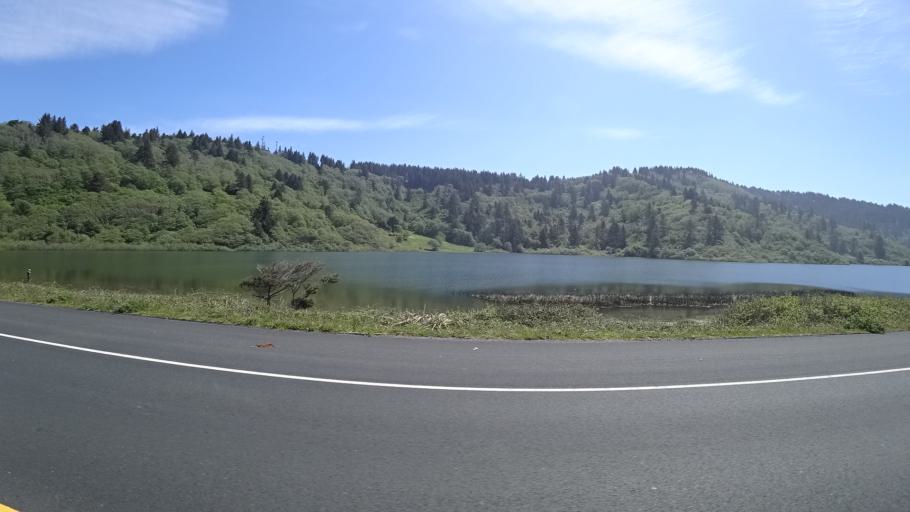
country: US
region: California
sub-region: Humboldt County
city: Westhaven-Moonstone
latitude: 41.2759
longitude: -124.0946
